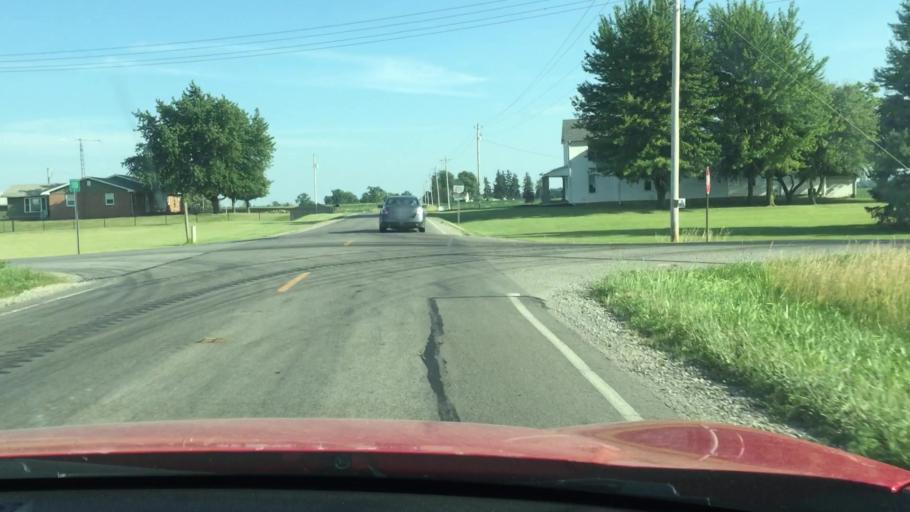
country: US
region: Ohio
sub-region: Hardin County
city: Ada
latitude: 40.6748
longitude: -83.8565
